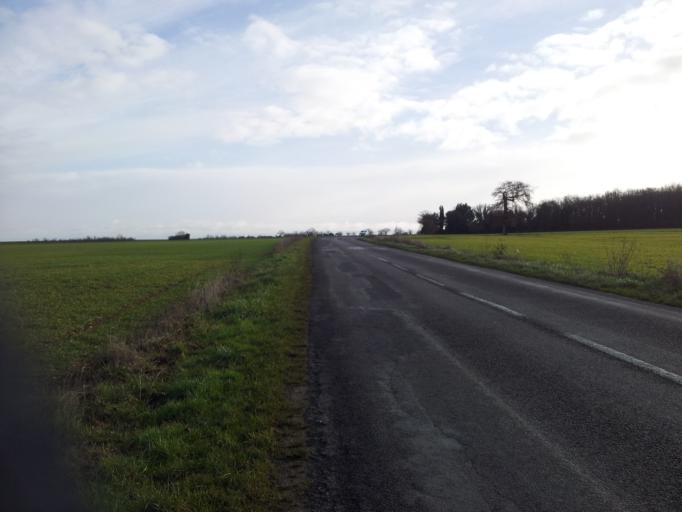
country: FR
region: Poitou-Charentes
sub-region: Departement de la Vienne
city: Avanton
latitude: 46.6616
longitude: 0.3206
